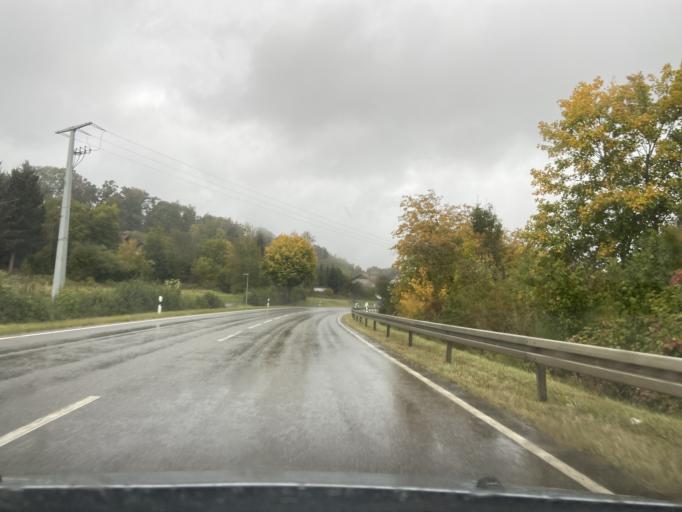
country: DE
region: Baden-Wuerttemberg
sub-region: Tuebingen Region
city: Scheer
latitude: 48.0647
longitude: 9.2984
